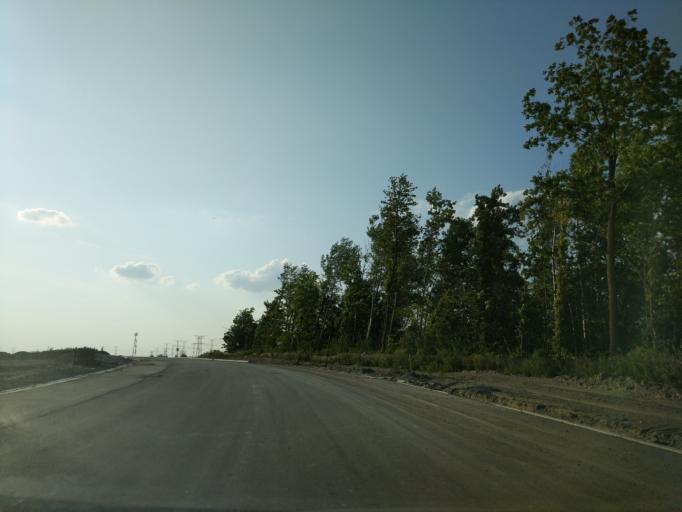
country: CA
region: Ontario
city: Markham
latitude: 43.8499
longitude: -79.2418
